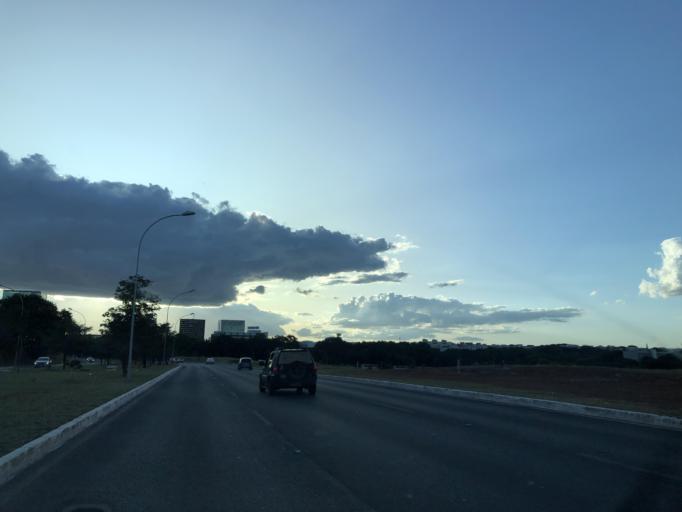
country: BR
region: Federal District
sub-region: Brasilia
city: Brasilia
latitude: -15.7895
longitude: -47.8775
